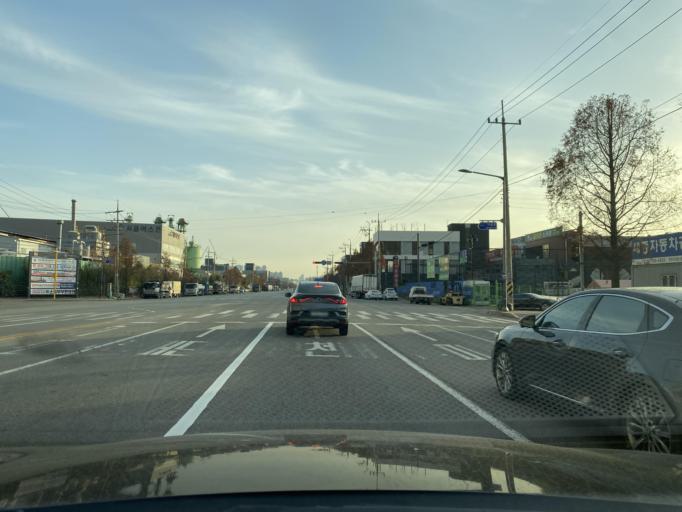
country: KR
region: Incheon
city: Incheon
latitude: 37.5042
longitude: 126.6616
